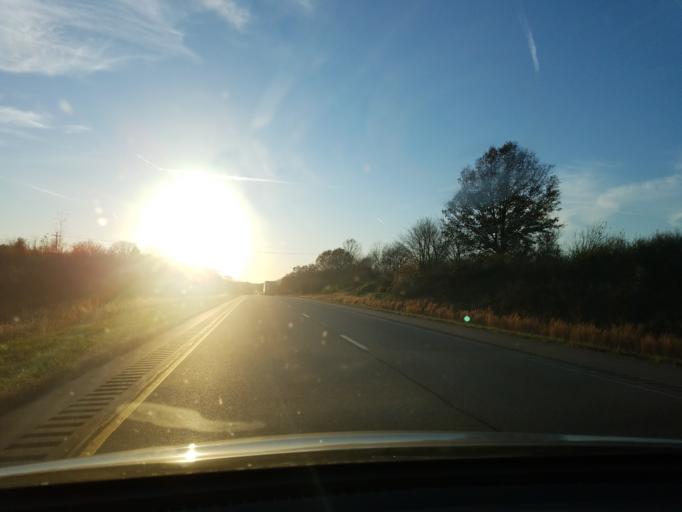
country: US
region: Indiana
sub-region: Warrick County
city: Chandler
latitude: 38.1796
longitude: -87.4045
